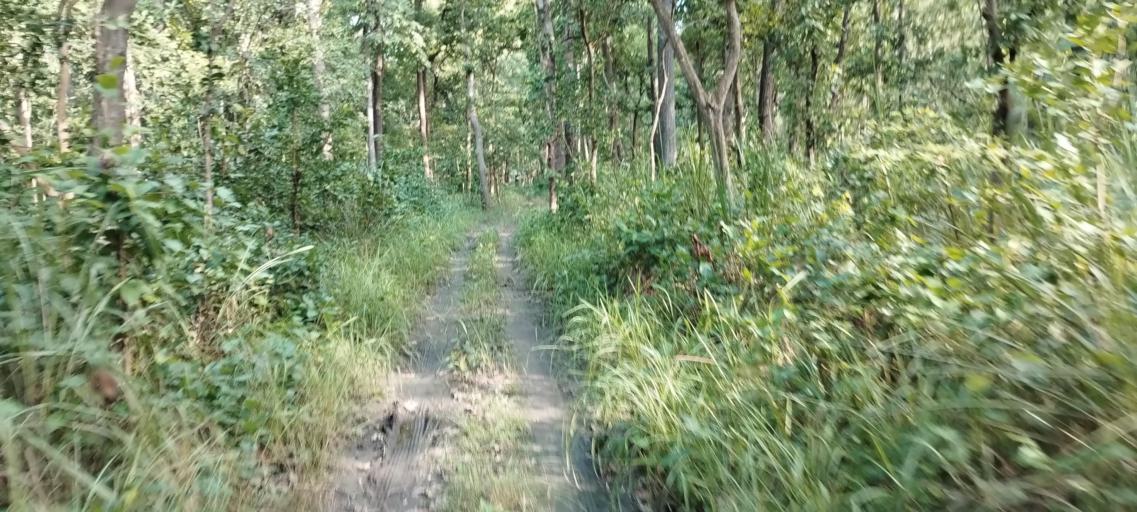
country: NP
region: Far Western
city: Tikapur
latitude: 28.5499
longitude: 81.2871
